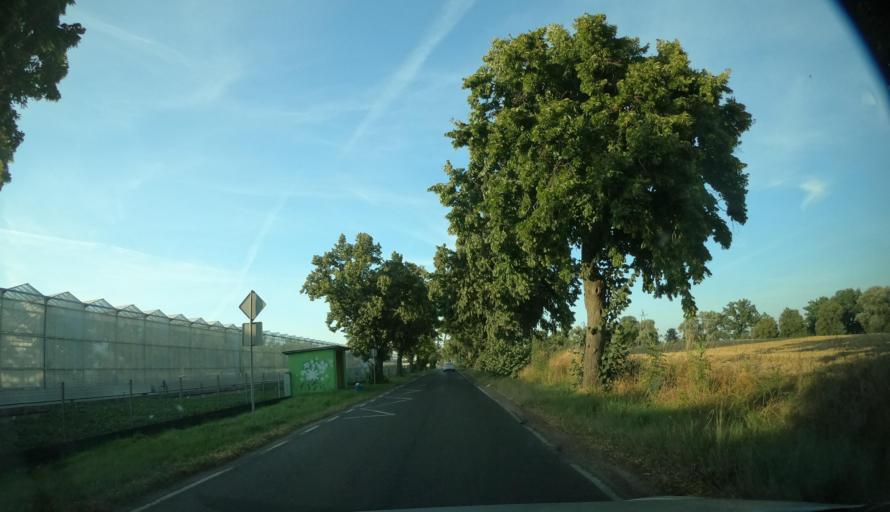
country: PL
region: Kujawsko-Pomorskie
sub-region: Powiat swiecki
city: Pruszcz
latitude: 53.2395
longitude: 18.2174
